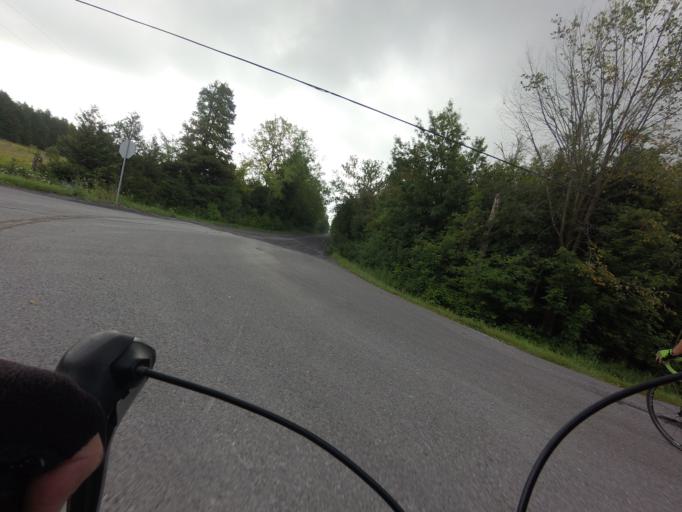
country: CA
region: Ontario
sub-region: Lanark County
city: Smiths Falls
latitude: 44.9510
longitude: -75.7858
